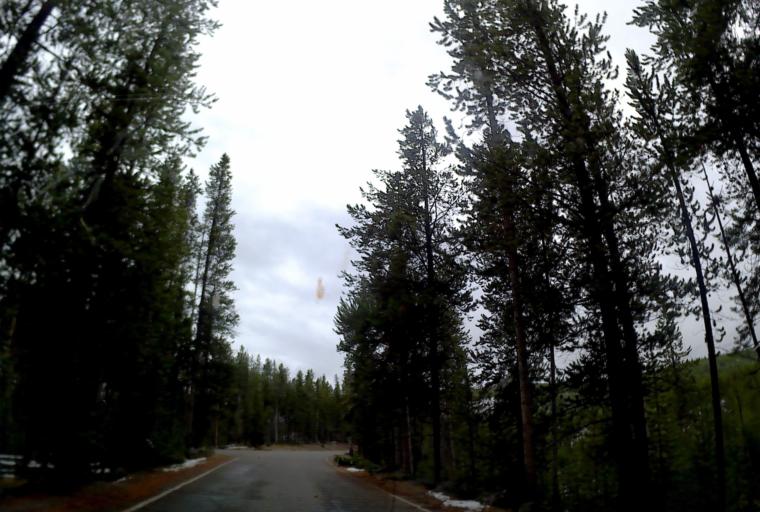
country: US
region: Montana
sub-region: Gallatin County
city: West Yellowstone
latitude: 44.6635
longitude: -111.1120
